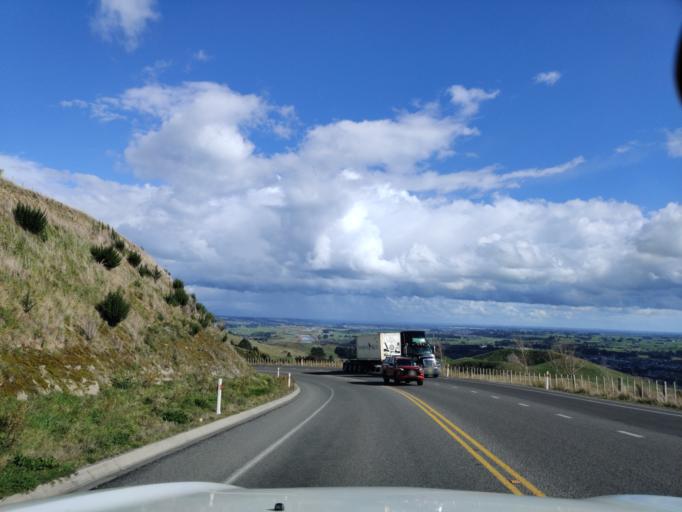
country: NZ
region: Manawatu-Wanganui
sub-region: Palmerston North City
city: Palmerston North
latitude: -40.2866
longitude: 175.7870
